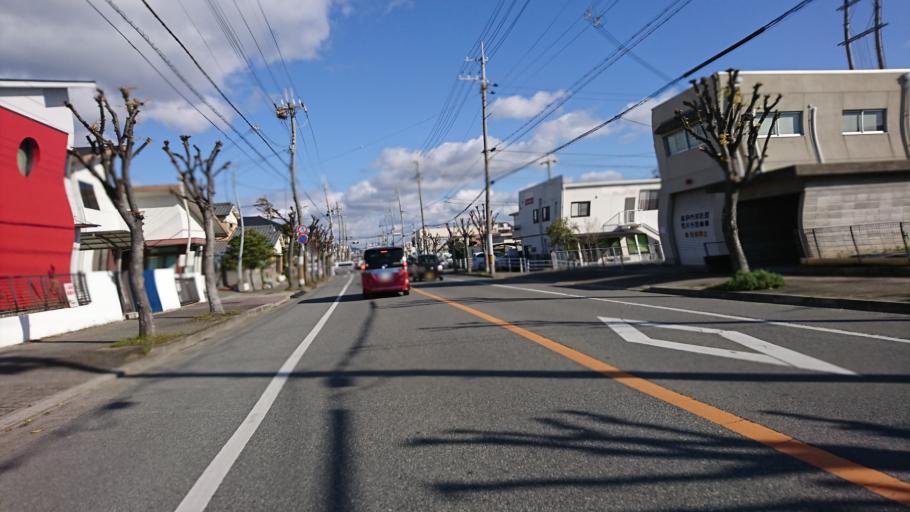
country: JP
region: Hyogo
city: Kakogawacho-honmachi
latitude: 34.7623
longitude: 134.7951
